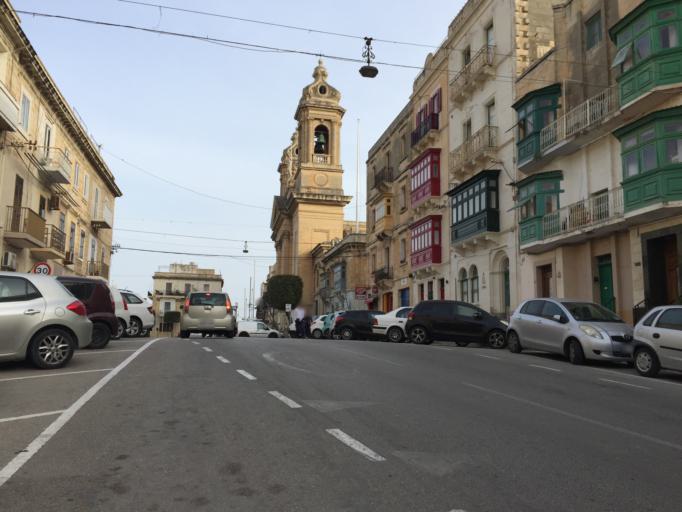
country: MT
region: L-Isla
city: Senglea
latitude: 35.8865
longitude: 14.5179
